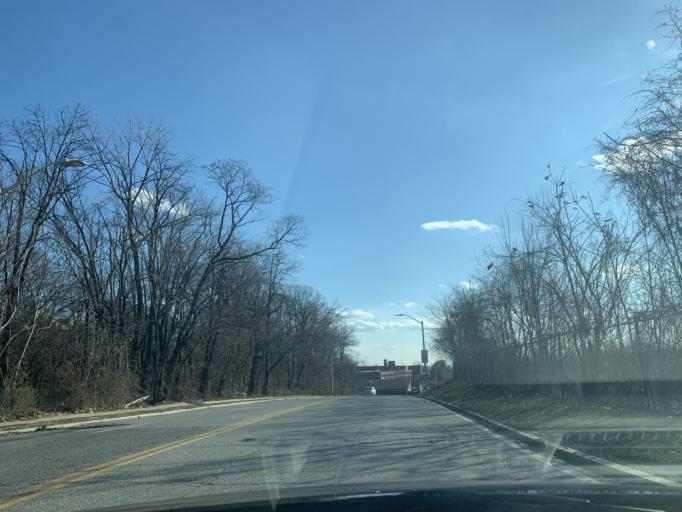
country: US
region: Maryland
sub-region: Baltimore County
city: Lochearn
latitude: 39.3217
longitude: -76.6653
